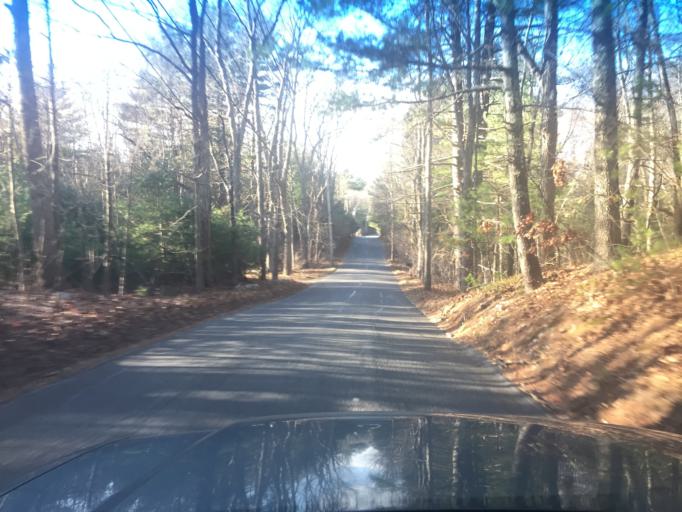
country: US
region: Massachusetts
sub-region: Middlesex County
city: Ashland
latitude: 42.2245
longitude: -71.4742
